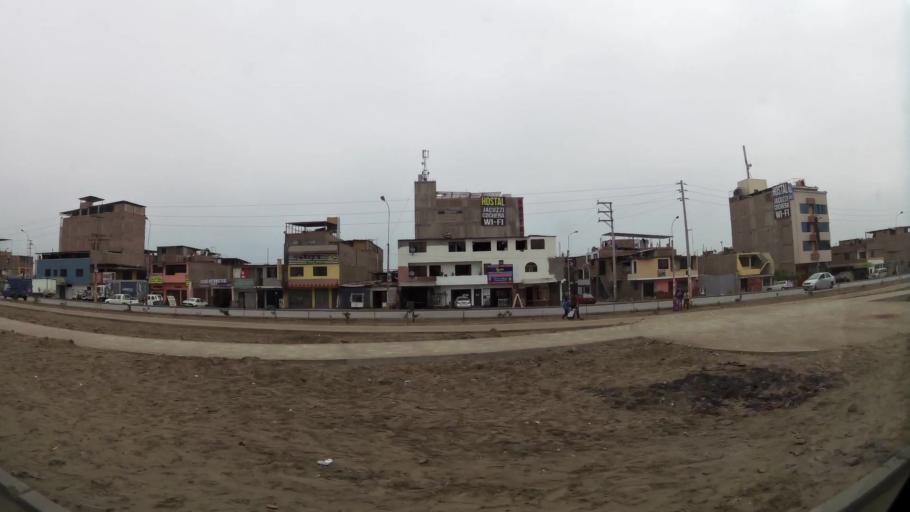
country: PE
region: Lima
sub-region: Lima
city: Surco
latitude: -12.2099
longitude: -76.9504
